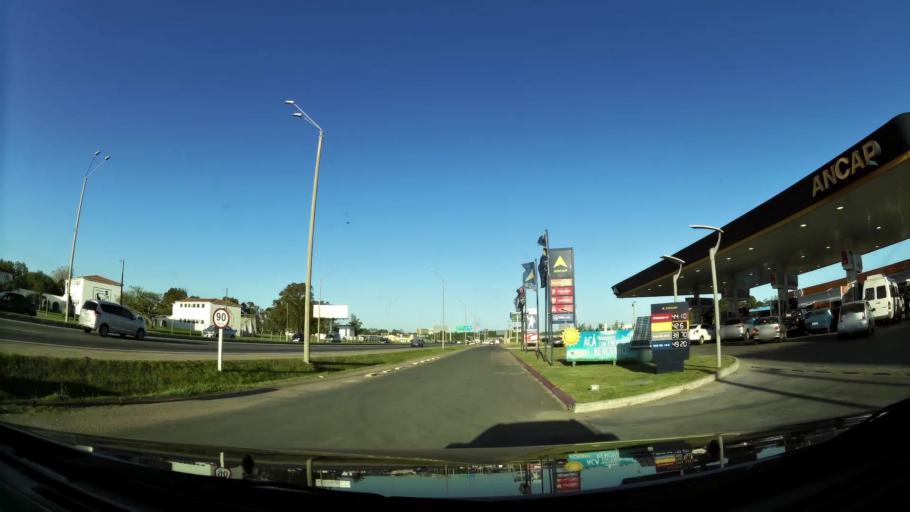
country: UY
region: Canelones
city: Barra de Carrasco
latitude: -34.8448
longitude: -56.0202
